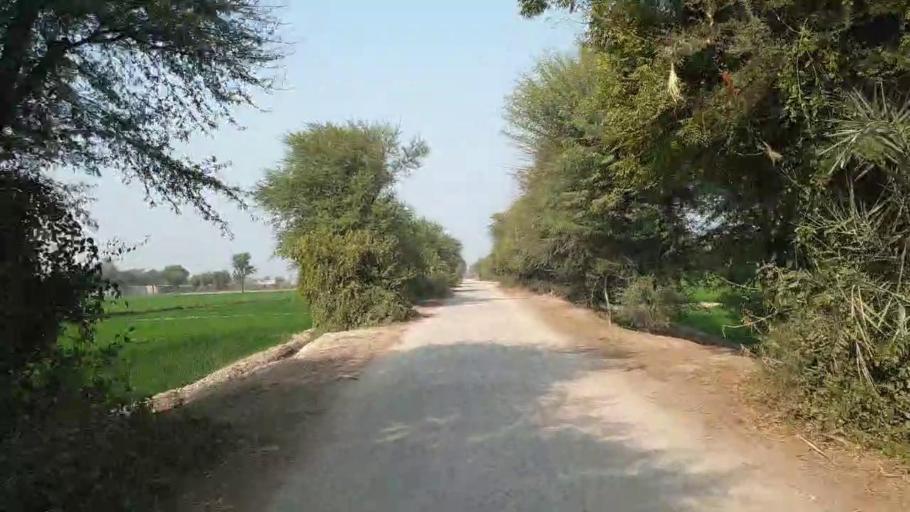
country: PK
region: Sindh
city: Hala
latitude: 25.8490
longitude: 68.4618
